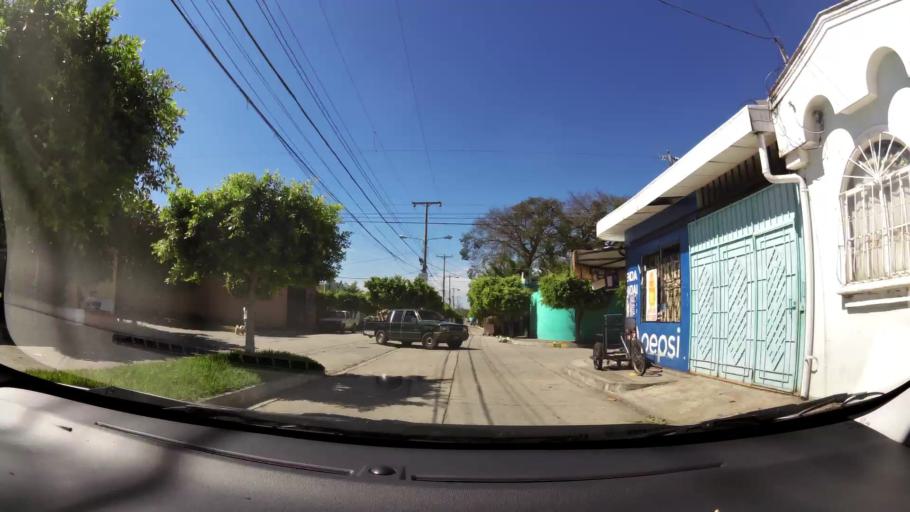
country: SV
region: La Libertad
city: San Juan Opico
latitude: 13.7976
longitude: -89.3541
